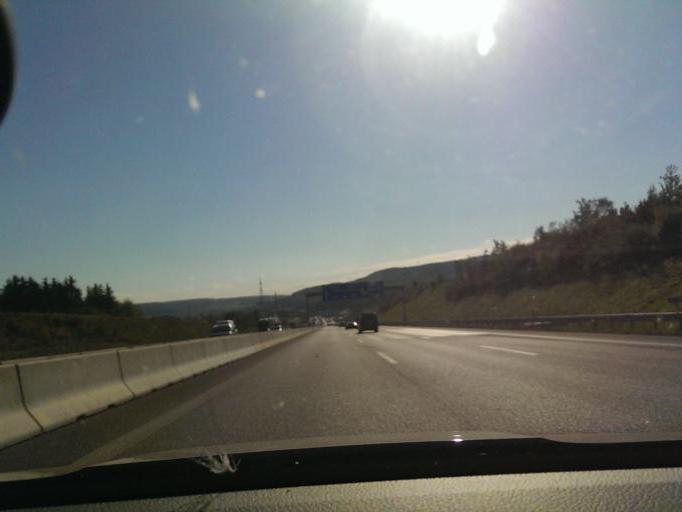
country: DE
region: Baden-Wuerttemberg
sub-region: Regierungsbezirk Stuttgart
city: Rutesheim
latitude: 48.7939
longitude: 8.9647
